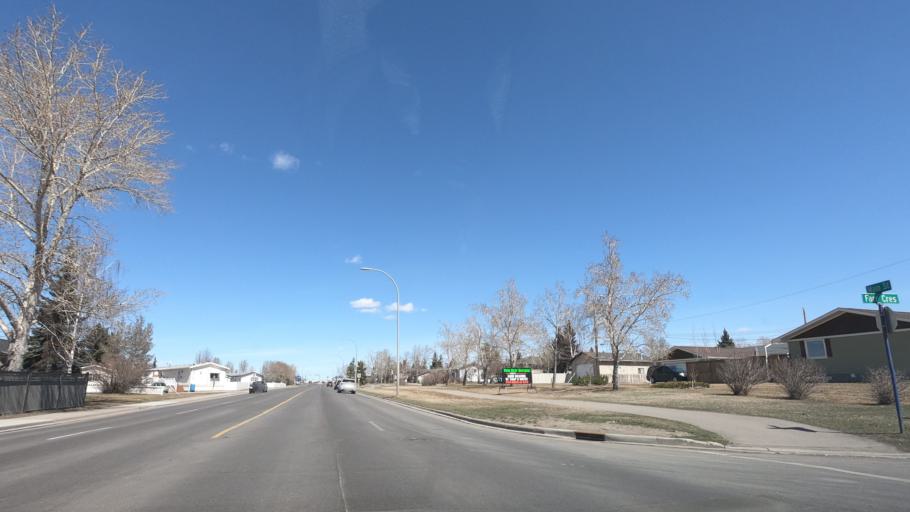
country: CA
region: Alberta
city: Airdrie
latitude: 51.2963
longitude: -114.0134
